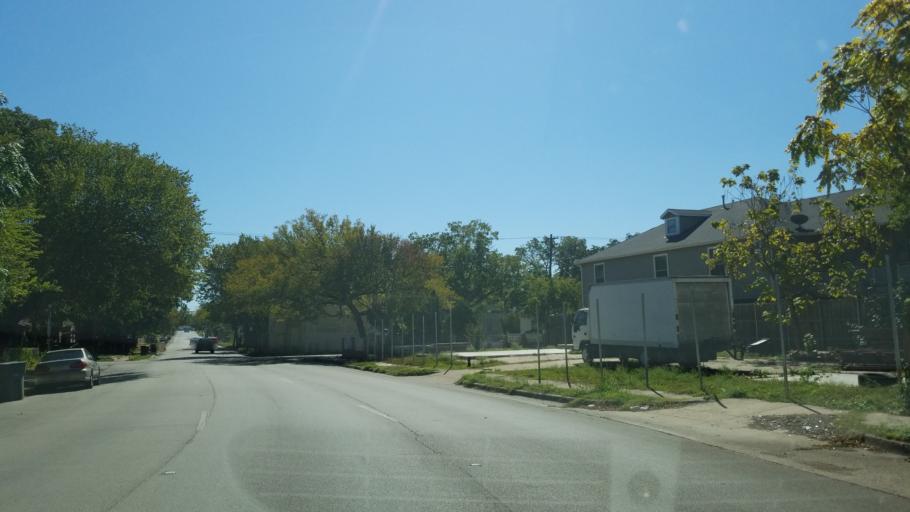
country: US
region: Texas
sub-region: Dallas County
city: Highland Park
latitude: 32.7978
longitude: -96.7536
